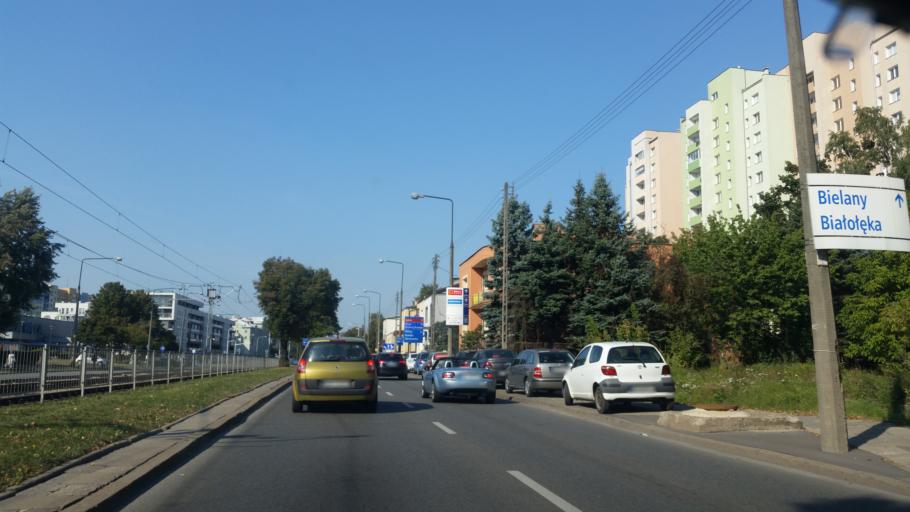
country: PL
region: Masovian Voivodeship
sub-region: Warszawa
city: Bemowo
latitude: 52.2273
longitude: 20.9159
